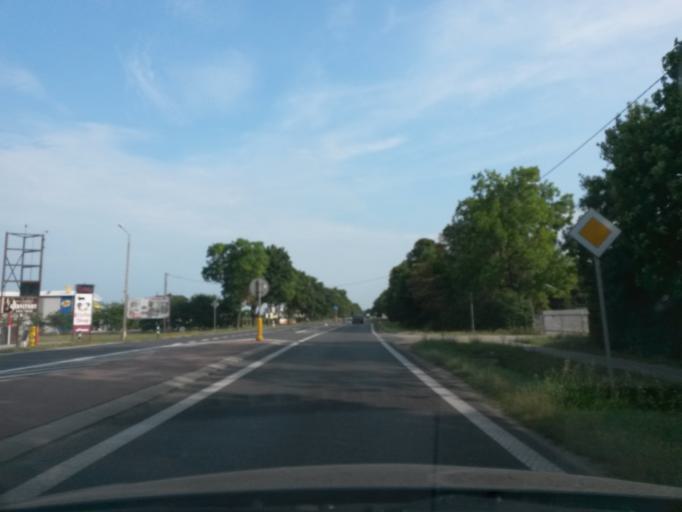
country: PL
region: Masovian Voivodeship
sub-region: Powiat sierpecki
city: Sierpc
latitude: 52.8599
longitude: 19.6788
